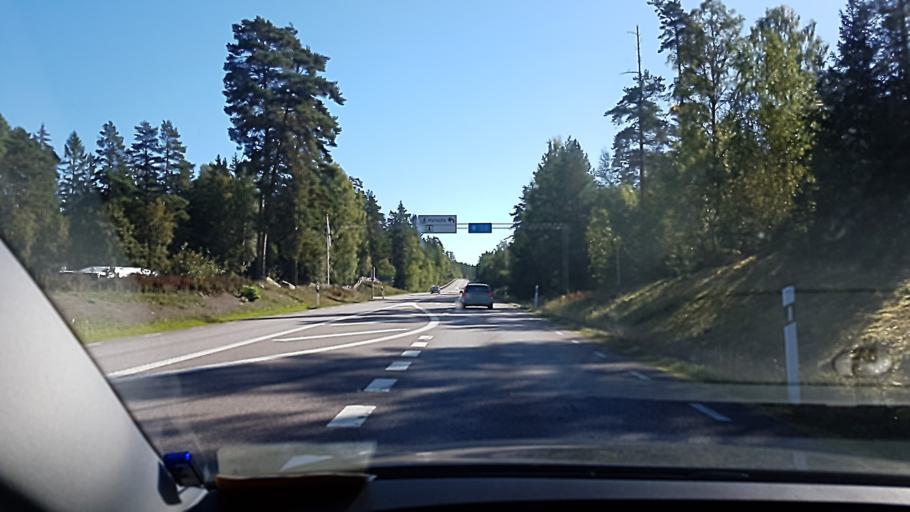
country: SE
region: Kronoberg
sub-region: Lessebo Kommun
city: Lessebo
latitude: 56.7817
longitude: 15.2303
